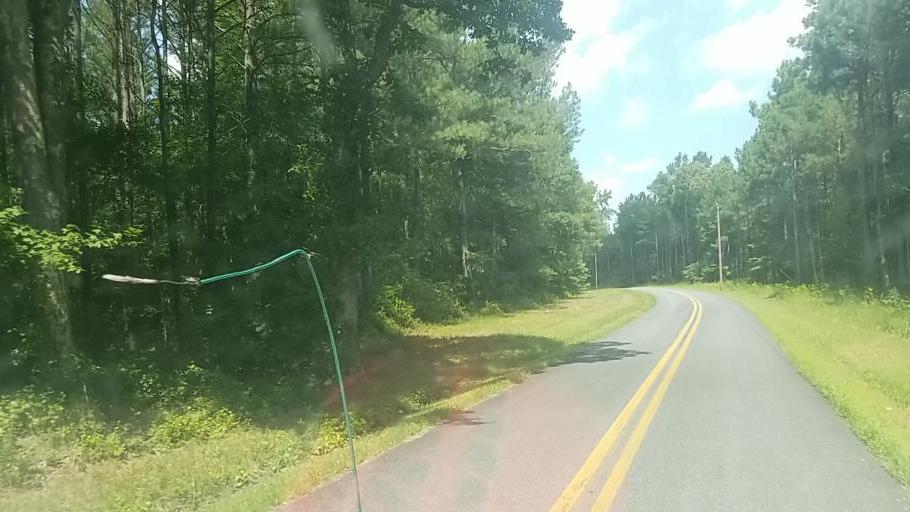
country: US
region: Maryland
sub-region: Worcester County
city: Snow Hill
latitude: 38.2517
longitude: -75.4337
